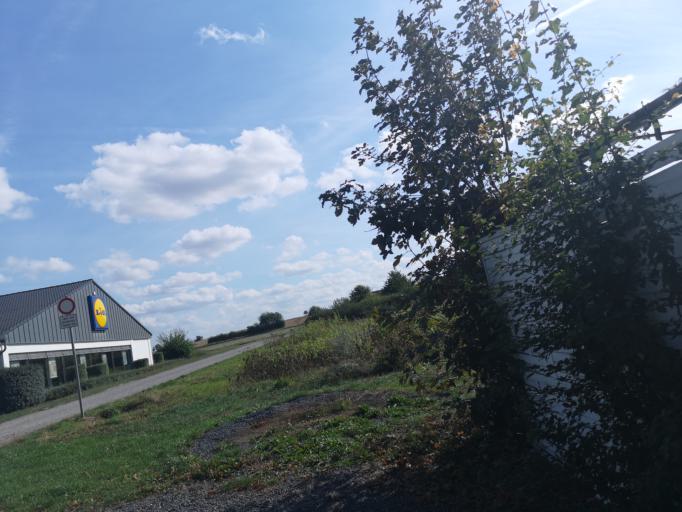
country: DE
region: North Rhine-Westphalia
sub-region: Regierungsbezirk Koln
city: Nideggen
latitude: 50.6955
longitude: 6.4895
